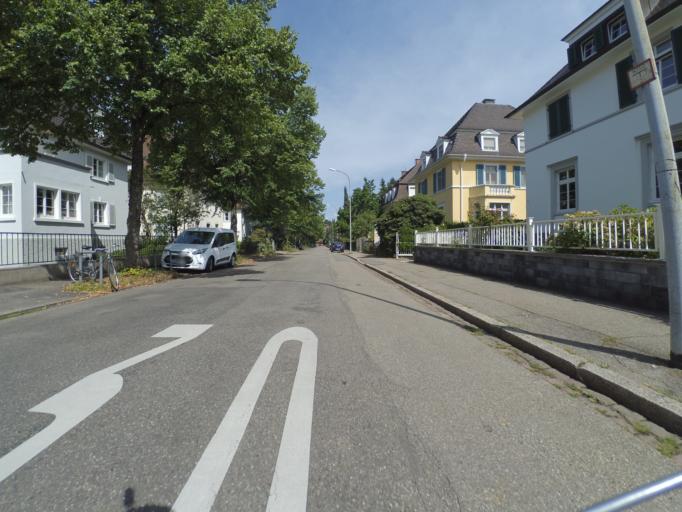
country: DE
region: Baden-Wuerttemberg
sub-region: Freiburg Region
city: Freiburg
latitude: 48.0092
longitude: 7.8628
